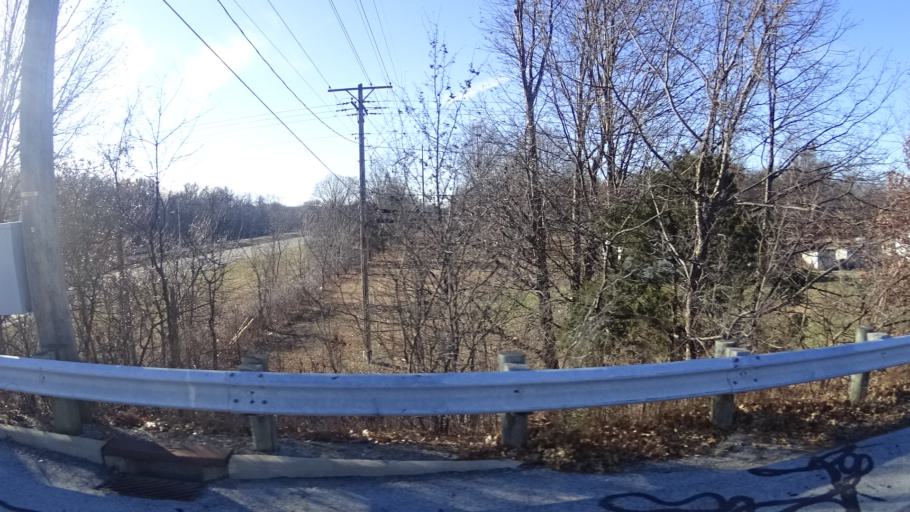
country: US
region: Ohio
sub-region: Lorain County
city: Vermilion
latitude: 41.4031
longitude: -82.3414
